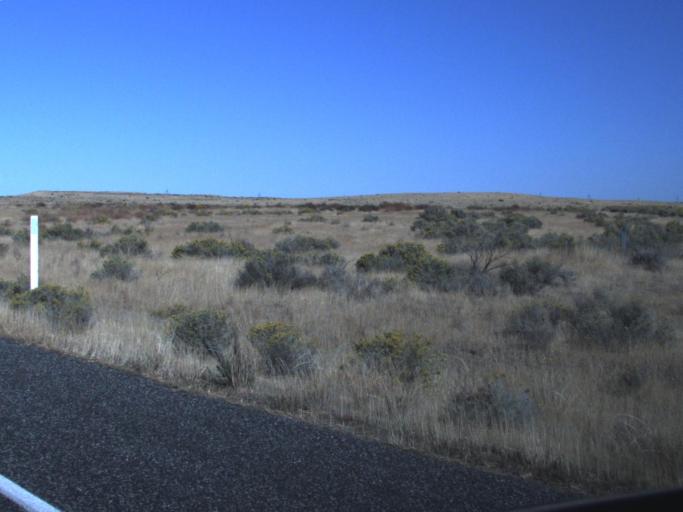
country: US
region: Washington
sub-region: Benton County
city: West Richland
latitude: 46.3788
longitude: -119.4146
